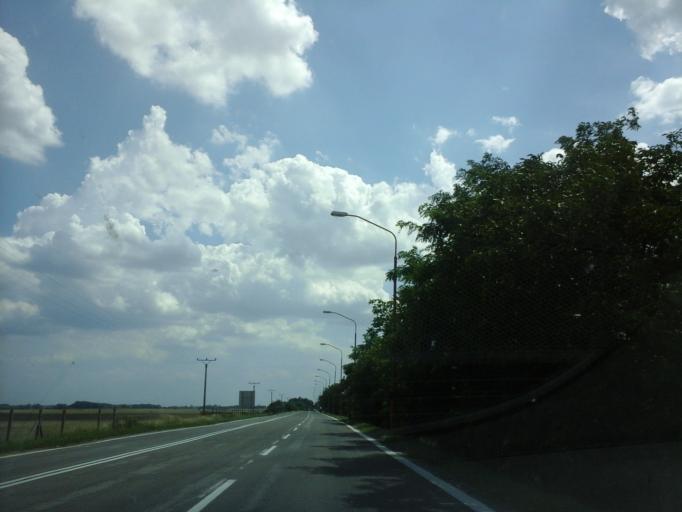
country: HU
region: Gyor-Moson-Sopron
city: Rajka
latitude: 48.0256
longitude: 17.1706
